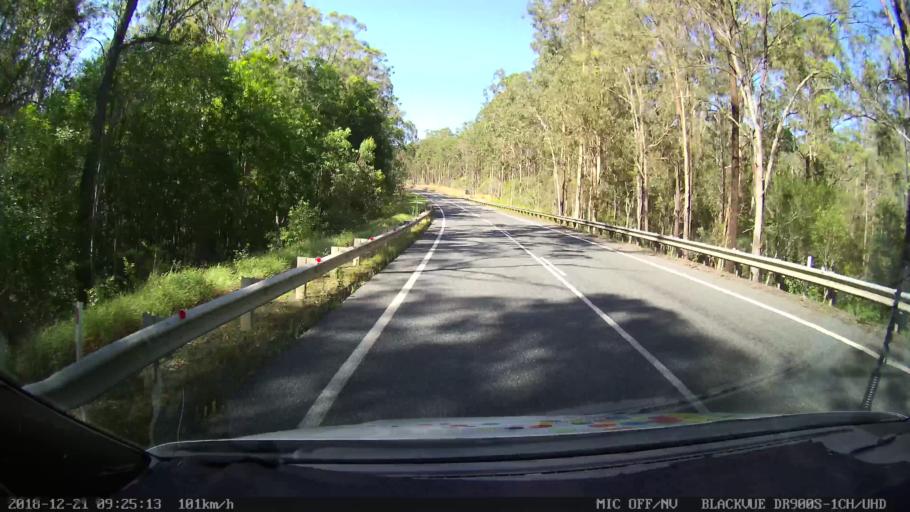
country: AU
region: New South Wales
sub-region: Clarence Valley
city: Maclean
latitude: -29.3766
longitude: 153.0096
